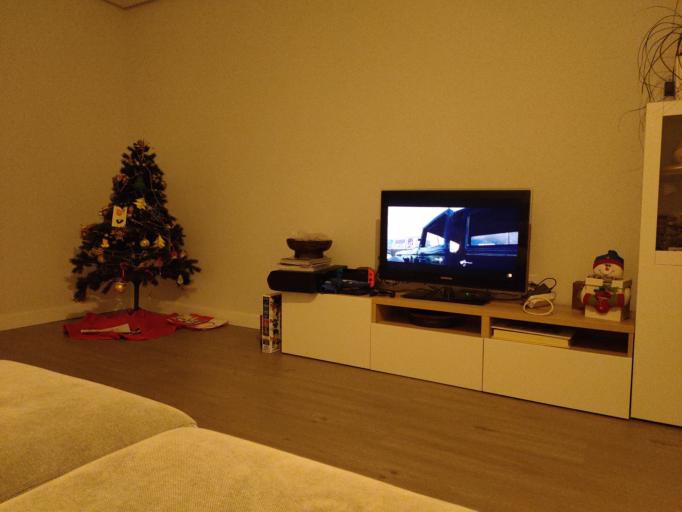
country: ES
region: Madrid
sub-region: Provincia de Madrid
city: Majadahonda
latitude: 40.4465
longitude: -3.8628
